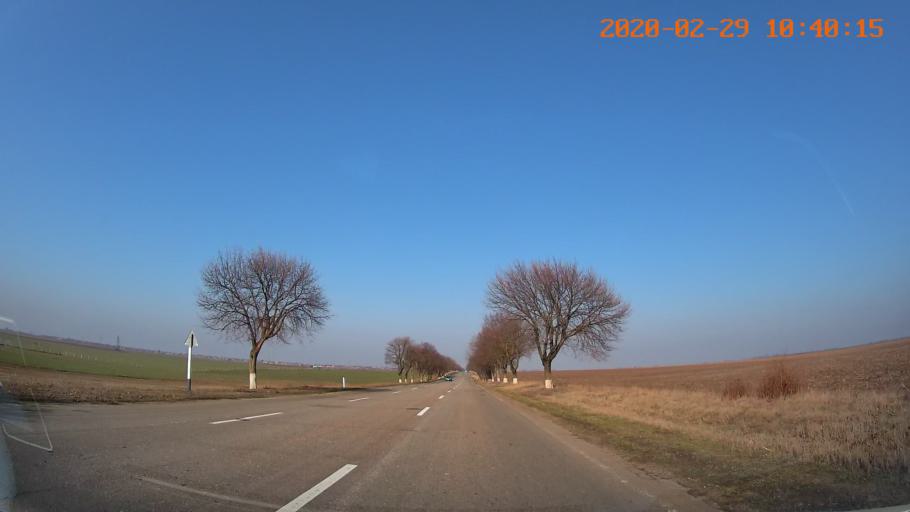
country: MD
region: Anenii Noi
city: Varnita
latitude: 47.0313
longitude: 29.4424
